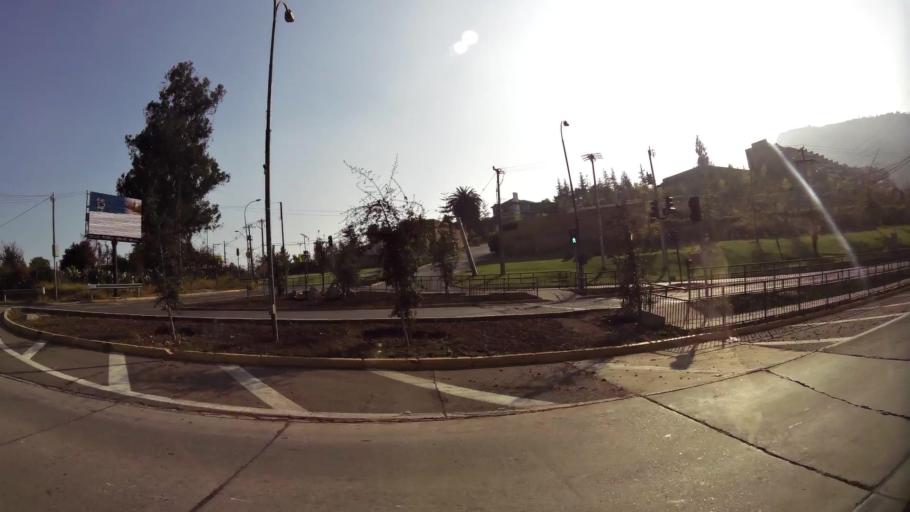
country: CL
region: Santiago Metropolitan
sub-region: Provincia de Santiago
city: Villa Presidente Frei, Nunoa, Santiago, Chile
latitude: -33.3664
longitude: -70.5448
